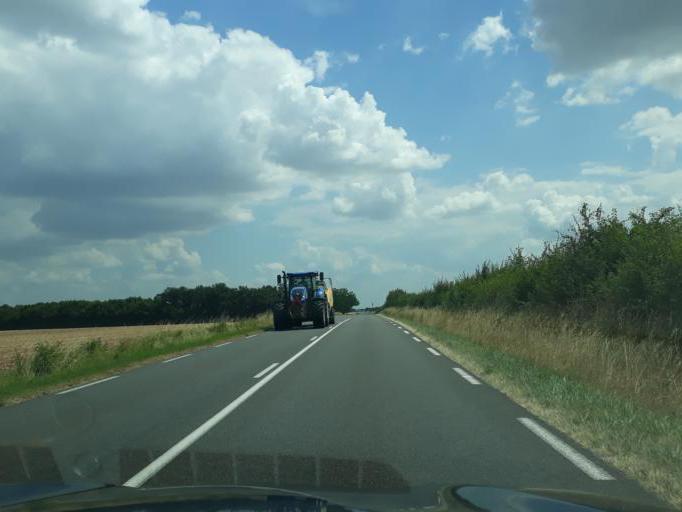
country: FR
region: Centre
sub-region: Departement du Cher
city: Avord
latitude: 47.0396
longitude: 2.5849
